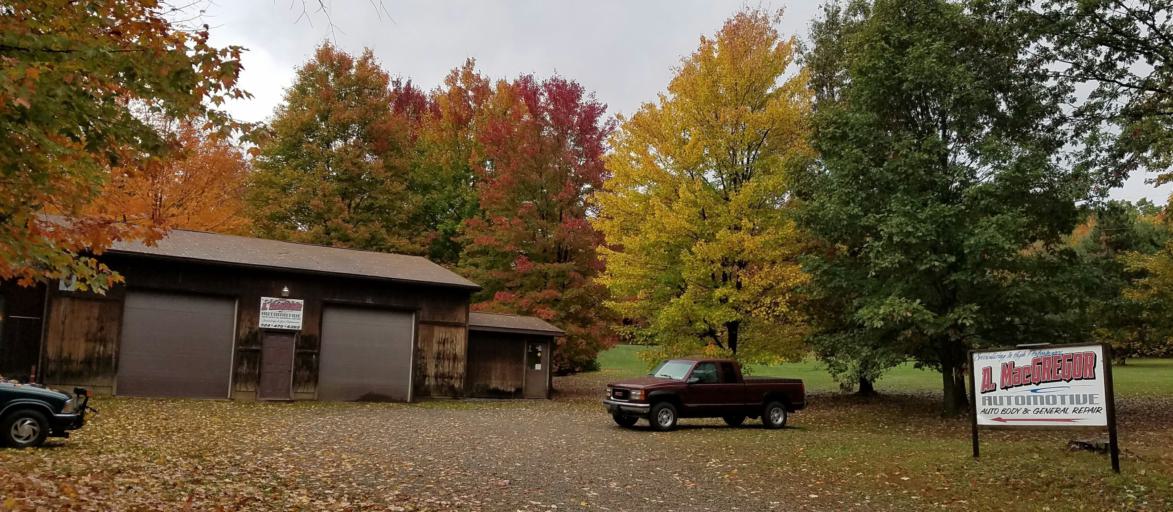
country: US
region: Pennsylvania
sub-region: Mercer County
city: Mercer
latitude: 41.3487
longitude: -80.2550
